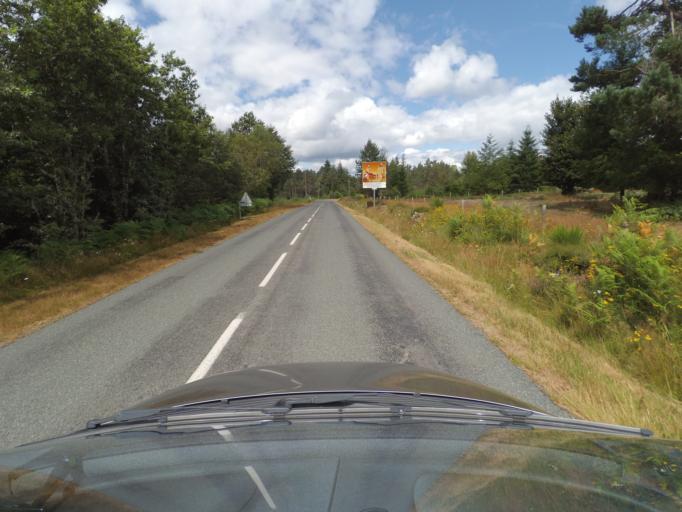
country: FR
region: Limousin
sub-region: Departement de la Haute-Vienne
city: Peyrat-le-Chateau
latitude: 45.8540
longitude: 1.9024
